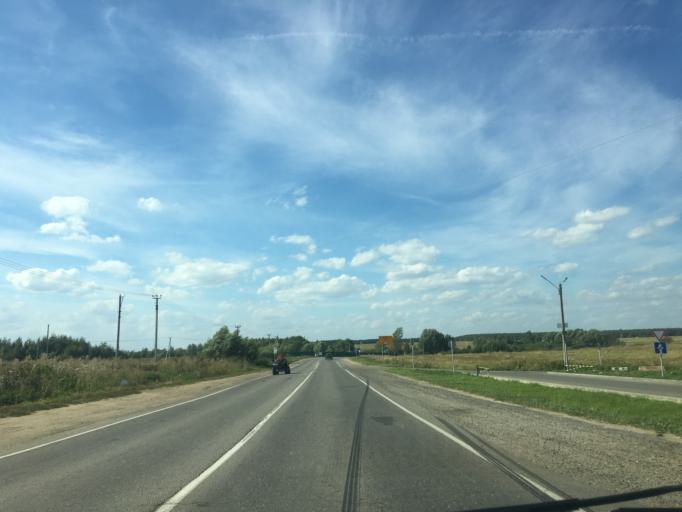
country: RU
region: Moskovskaya
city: Yam
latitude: 55.4770
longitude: 37.6661
